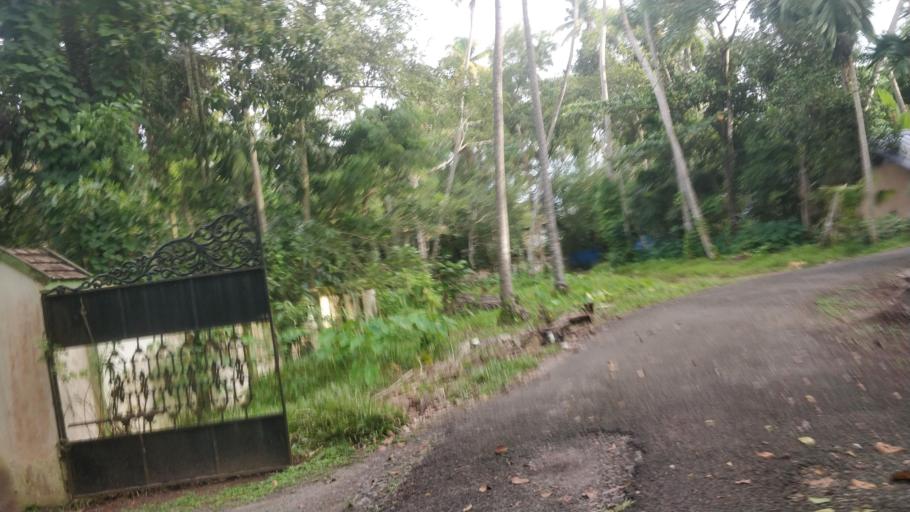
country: IN
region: Kerala
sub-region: Alappuzha
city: Shertallai
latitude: 9.6940
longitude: 76.3643
